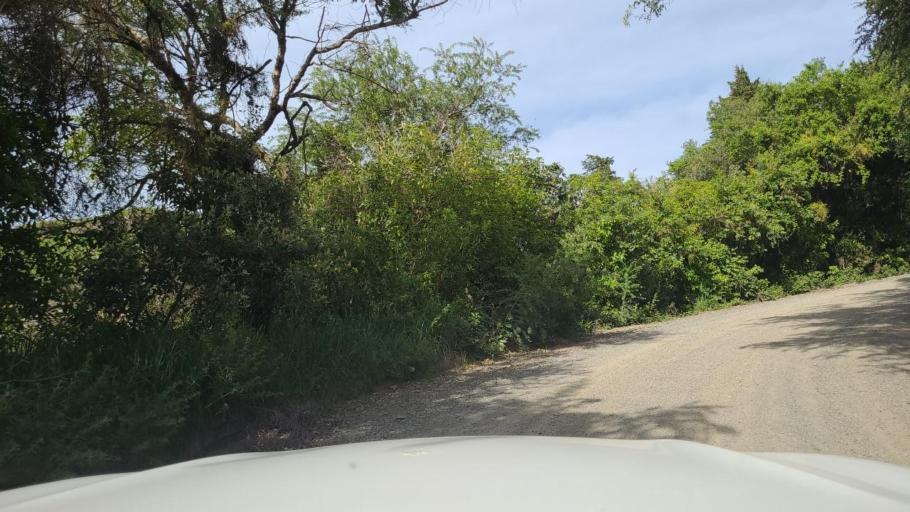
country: NZ
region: Hawke's Bay
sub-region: Napier City
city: Taradale
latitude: -39.3403
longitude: 176.6647
